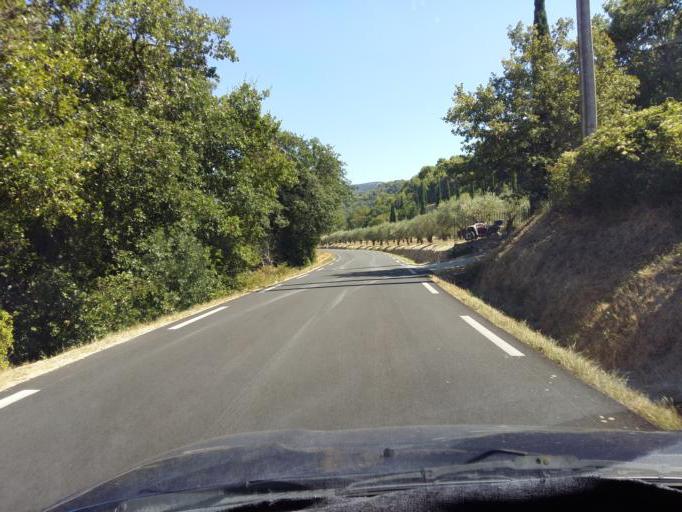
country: FR
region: Provence-Alpes-Cote d'Azur
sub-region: Departement du Vaucluse
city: Venasque
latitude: 44.0061
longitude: 5.1403
